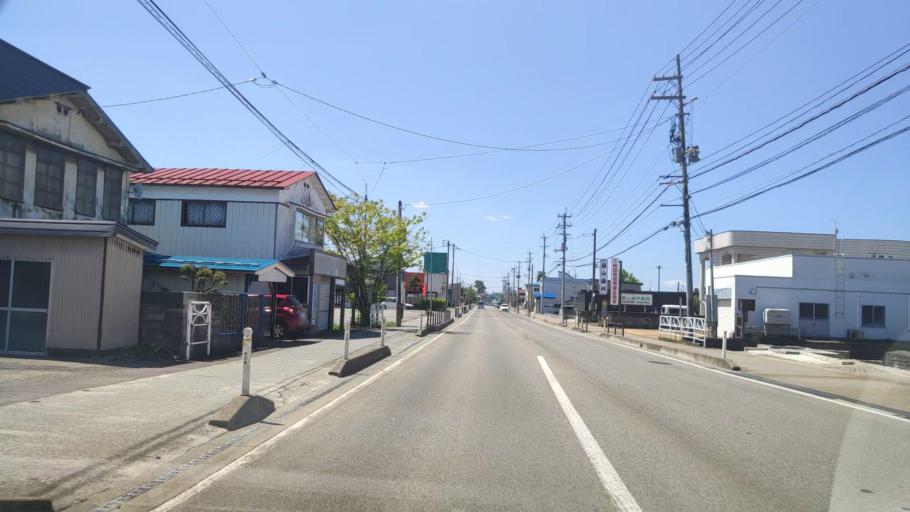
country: JP
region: Akita
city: Omagari
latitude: 39.4585
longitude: 140.4755
